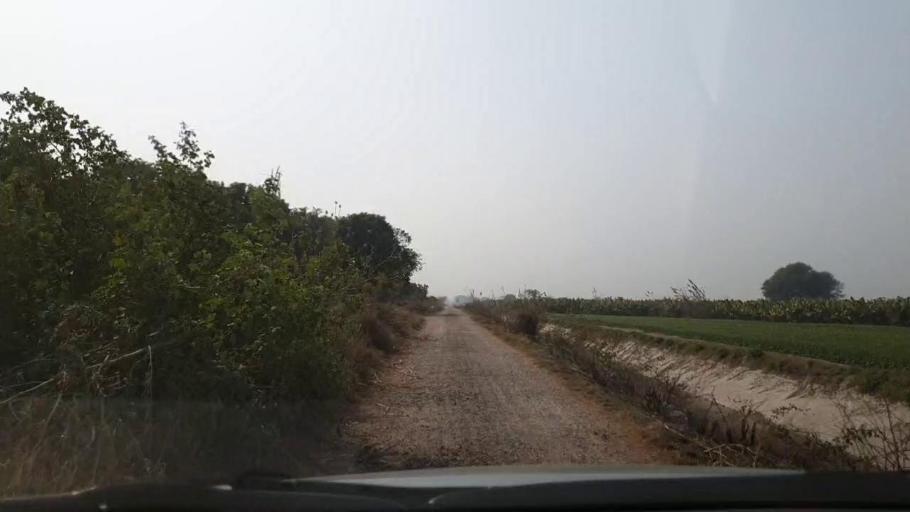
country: PK
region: Sindh
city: Matiari
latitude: 25.6405
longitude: 68.5145
